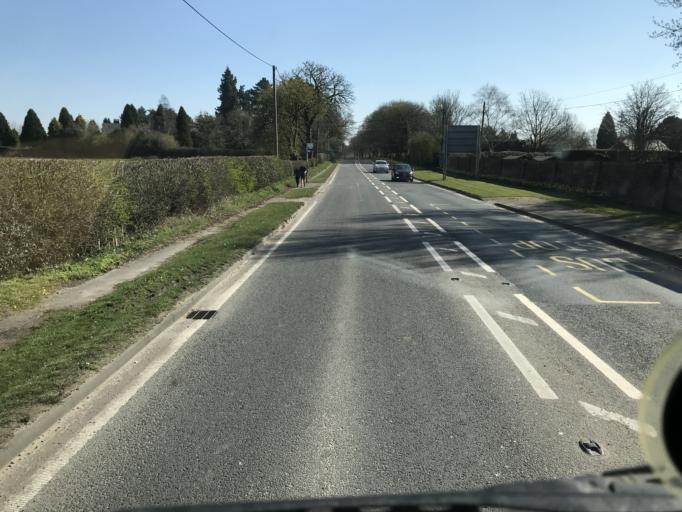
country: GB
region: England
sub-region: Cheshire East
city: Siddington
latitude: 53.2655
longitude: -2.2721
